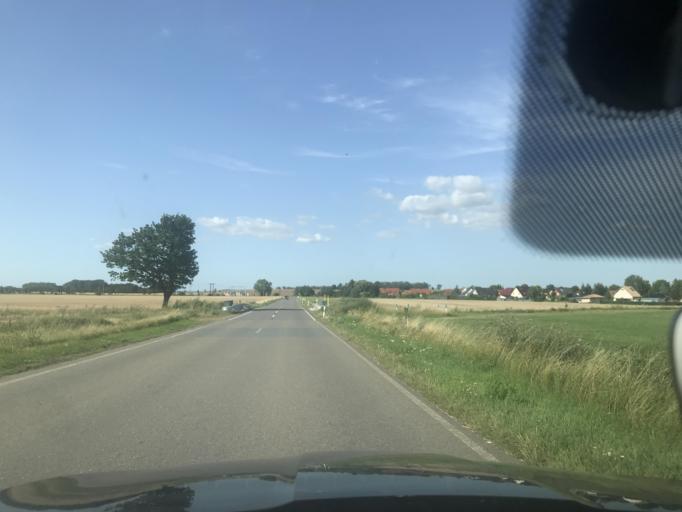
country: DE
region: Saxony-Anhalt
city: Wegeleben
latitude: 51.8857
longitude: 11.1621
